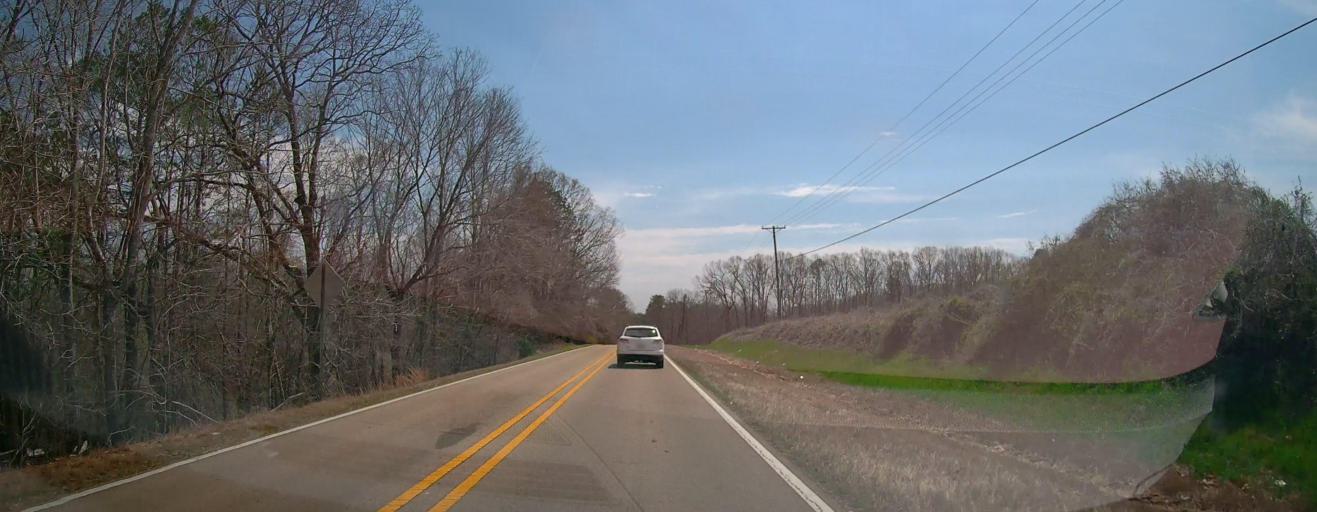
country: US
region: Mississippi
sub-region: Union County
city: New Albany
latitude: 34.4350
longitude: -88.9556
